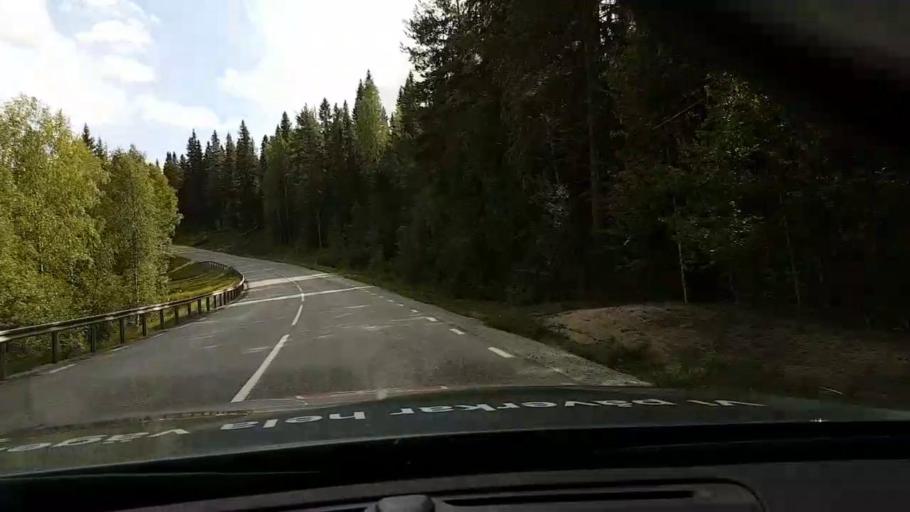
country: SE
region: Vaesternorrland
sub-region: OErnskoeldsviks Kommun
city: Bredbyn
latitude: 63.6436
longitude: 17.8966
